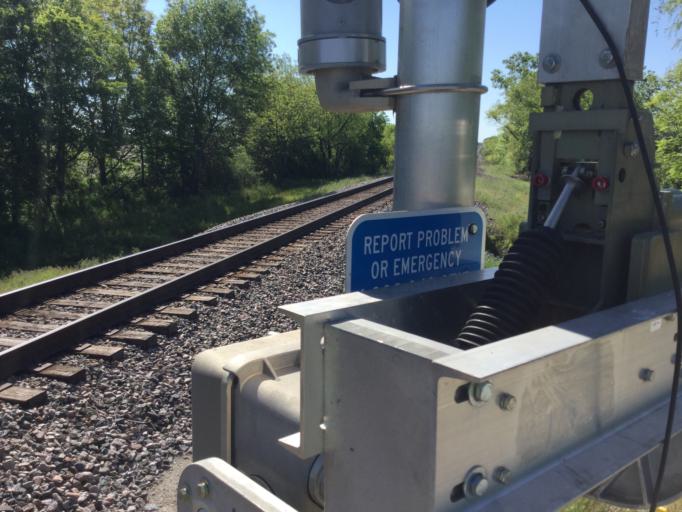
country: US
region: Kansas
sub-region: Labette County
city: Oswego
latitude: 37.2063
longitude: -95.1583
